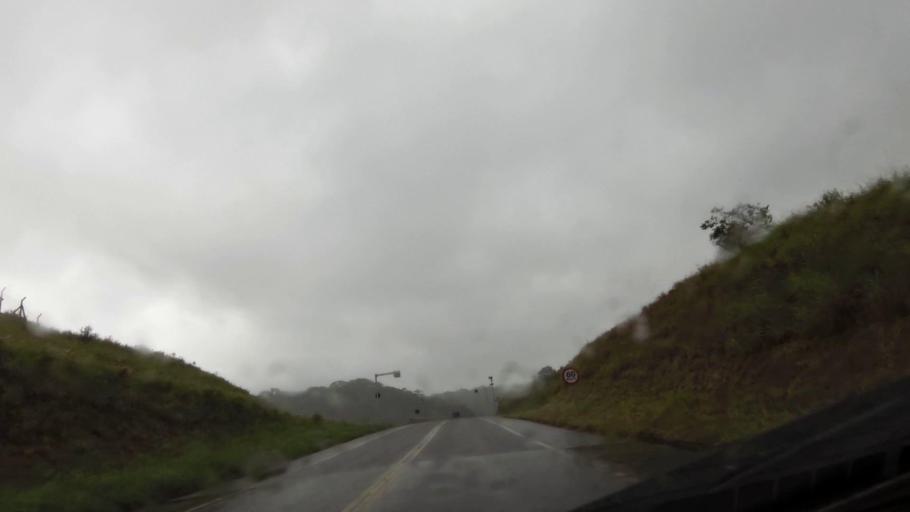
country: BR
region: Espirito Santo
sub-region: Guarapari
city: Guarapari
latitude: -20.6397
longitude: -40.5303
